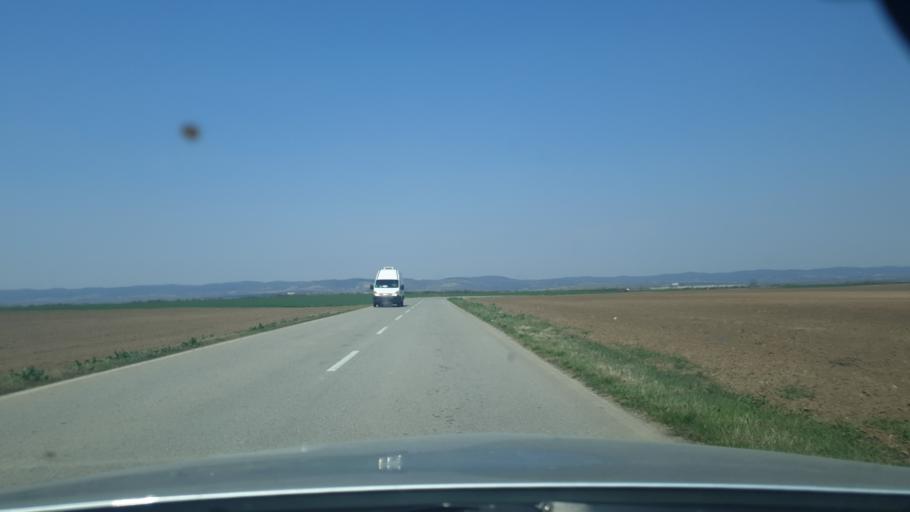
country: RS
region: Autonomna Pokrajina Vojvodina
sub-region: Sremski Okrug
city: Ruma
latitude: 45.0427
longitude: 19.7607
